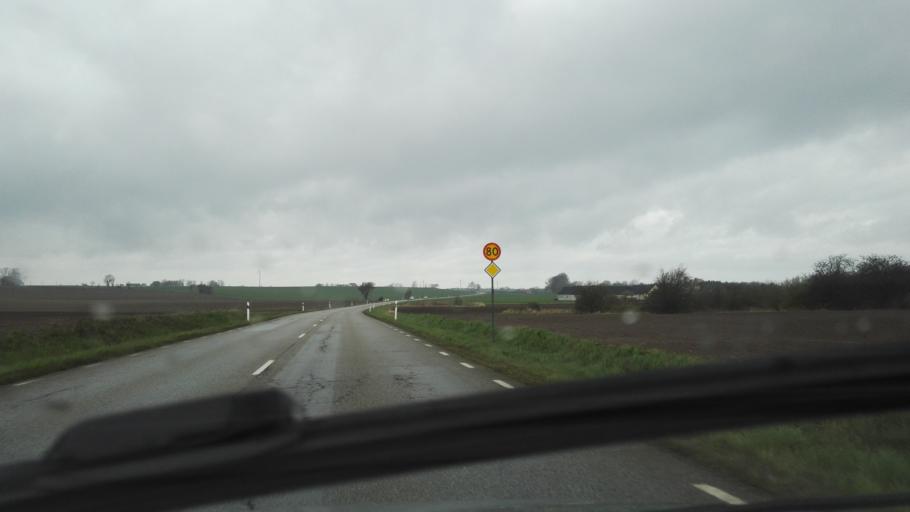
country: SE
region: Skane
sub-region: Simrishamns Kommun
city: Simrishamn
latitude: 55.5120
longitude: 14.3359
